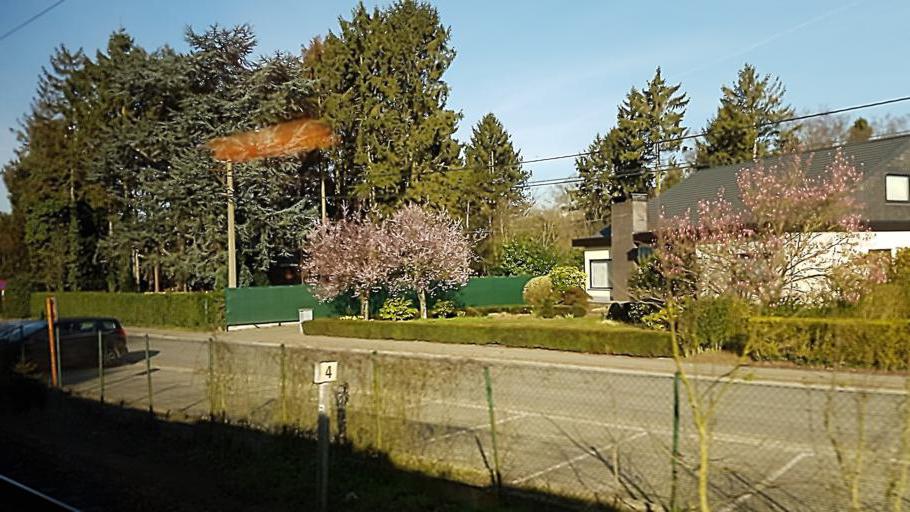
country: BE
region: Flanders
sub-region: Provincie Oost-Vlaanderen
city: De Pinte
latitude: 50.9961
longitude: 3.6477
